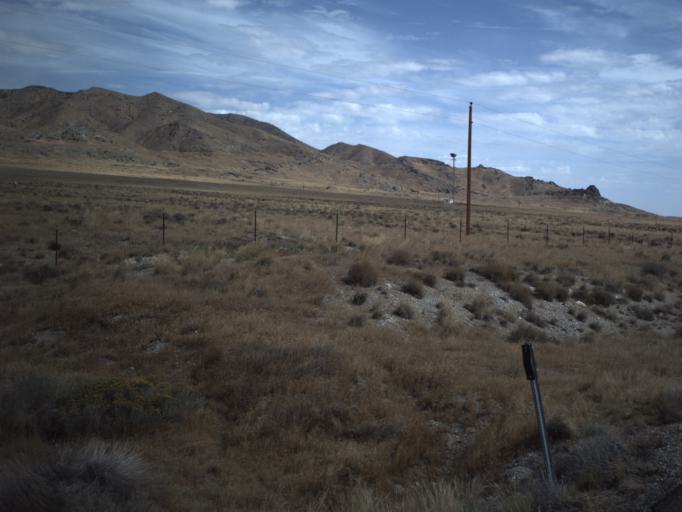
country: US
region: Utah
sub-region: Tooele County
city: Wendover
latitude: 41.4397
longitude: -113.7158
